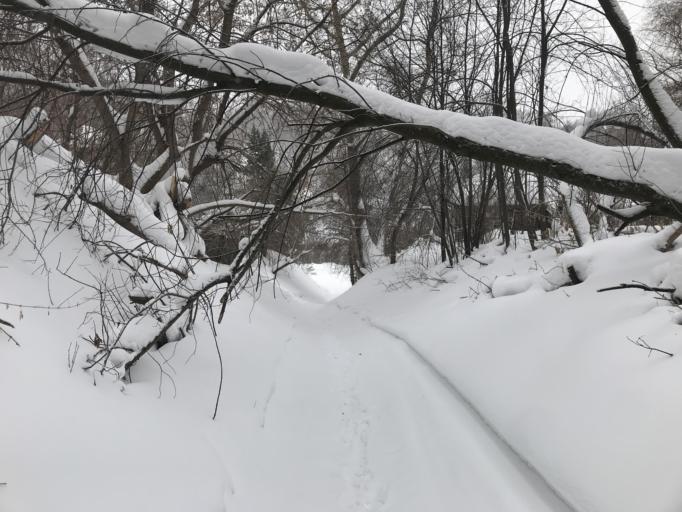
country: RU
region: Tjumen
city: Tobol'sk
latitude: 58.1990
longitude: 68.2591
